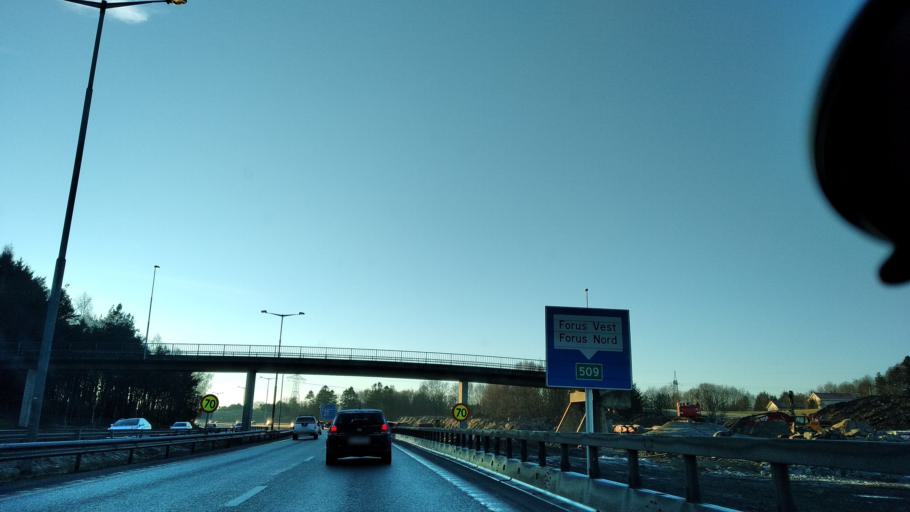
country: NO
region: Rogaland
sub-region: Sola
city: Sola
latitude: 58.9178
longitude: 5.6991
